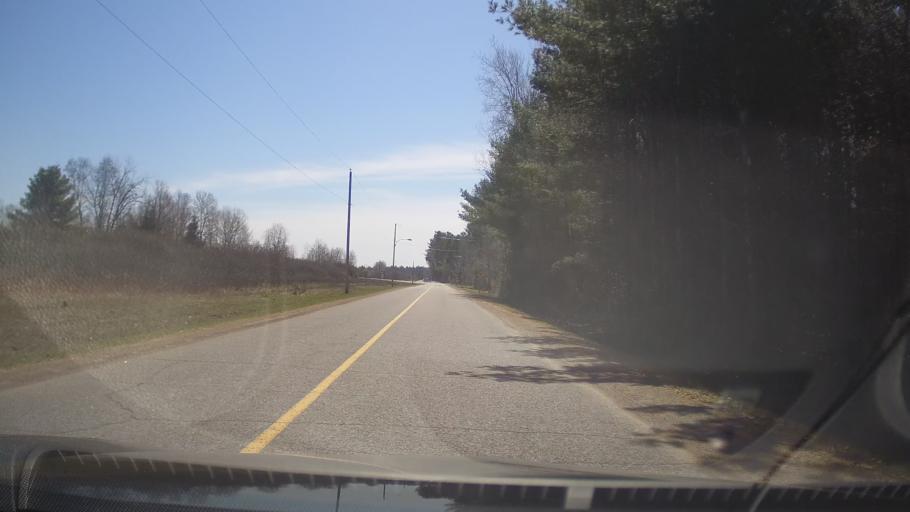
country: CA
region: Ontario
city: Arnprior
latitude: 45.5194
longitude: -76.4096
